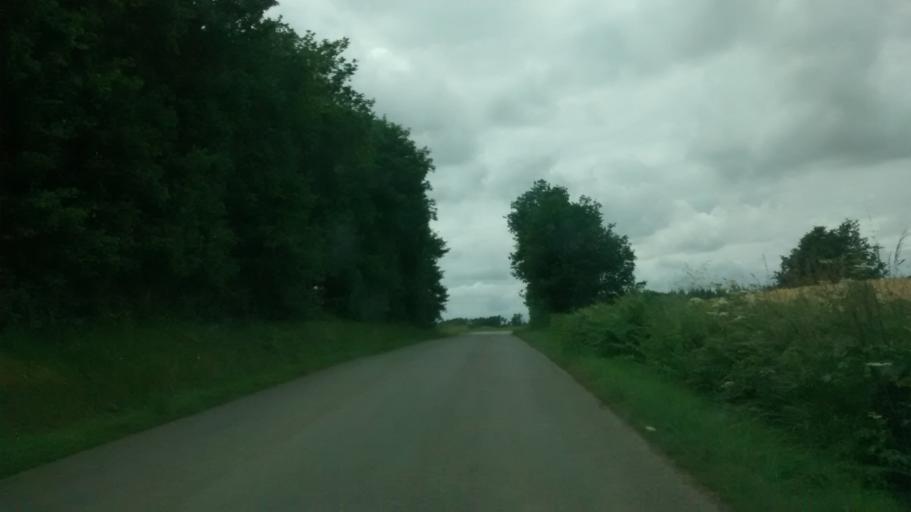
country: FR
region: Brittany
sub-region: Departement du Morbihan
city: Carentoir
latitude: 47.8259
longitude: -2.1681
